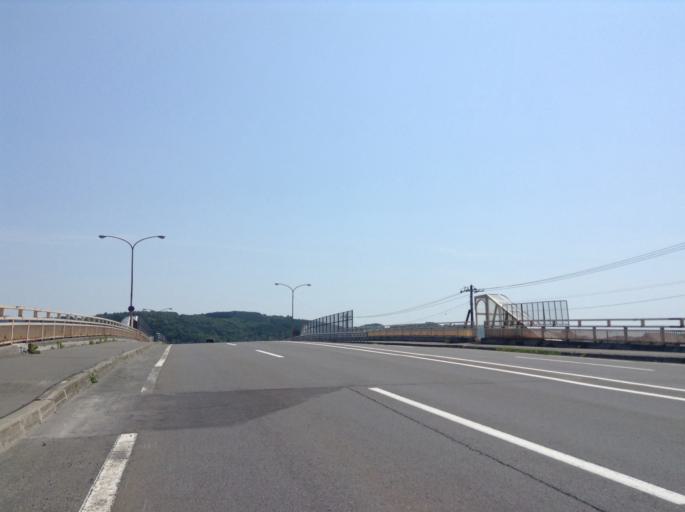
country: JP
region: Hokkaido
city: Nayoro
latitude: 44.3565
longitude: 142.4652
